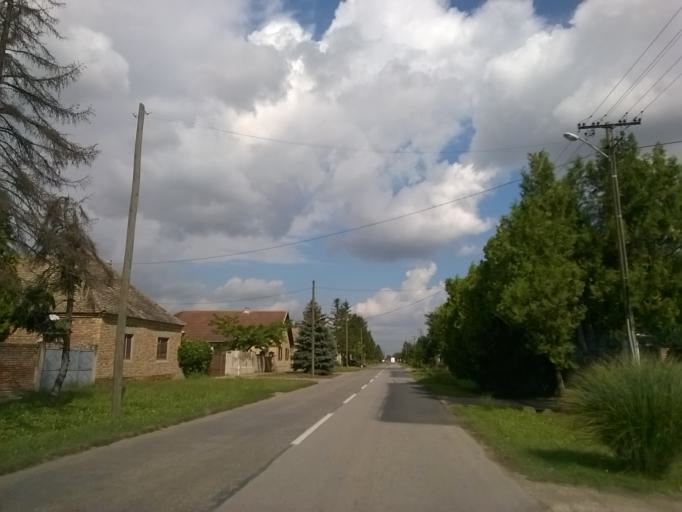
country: RS
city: Jermenovci
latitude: 45.1878
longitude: 21.0477
